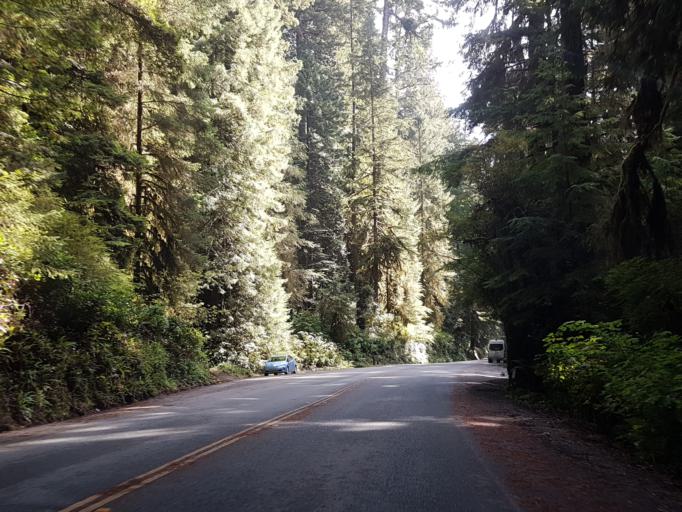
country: US
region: California
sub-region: Del Norte County
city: Bertsch-Oceanview
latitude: 41.4393
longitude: -124.0407
